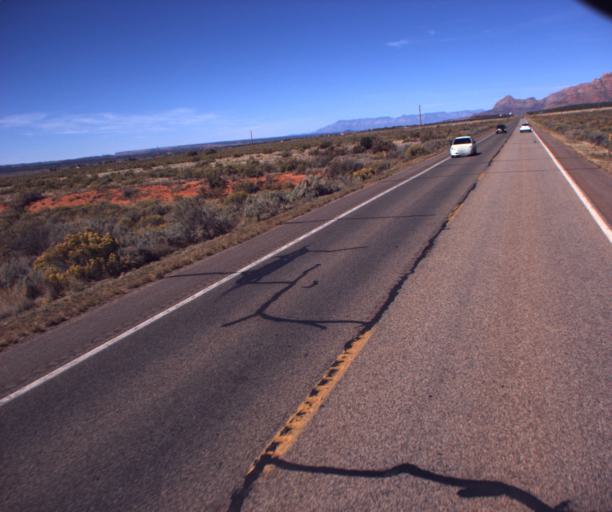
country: US
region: Arizona
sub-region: Mohave County
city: Colorado City
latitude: 36.9327
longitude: -112.9450
